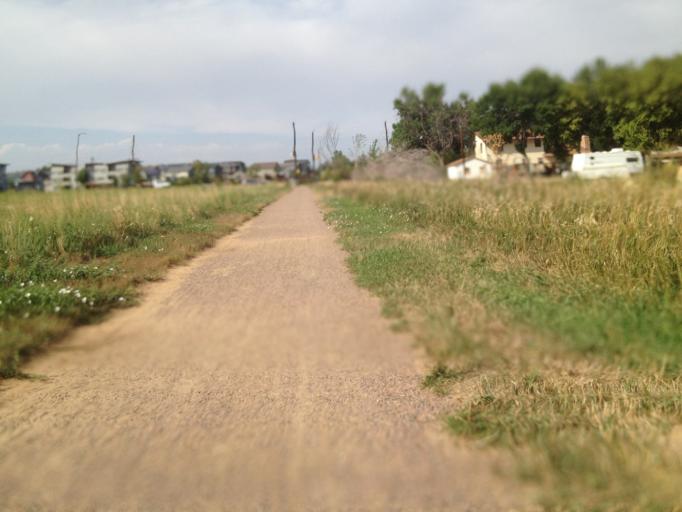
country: US
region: Colorado
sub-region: Boulder County
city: Louisville
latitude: 39.9858
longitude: -105.1188
